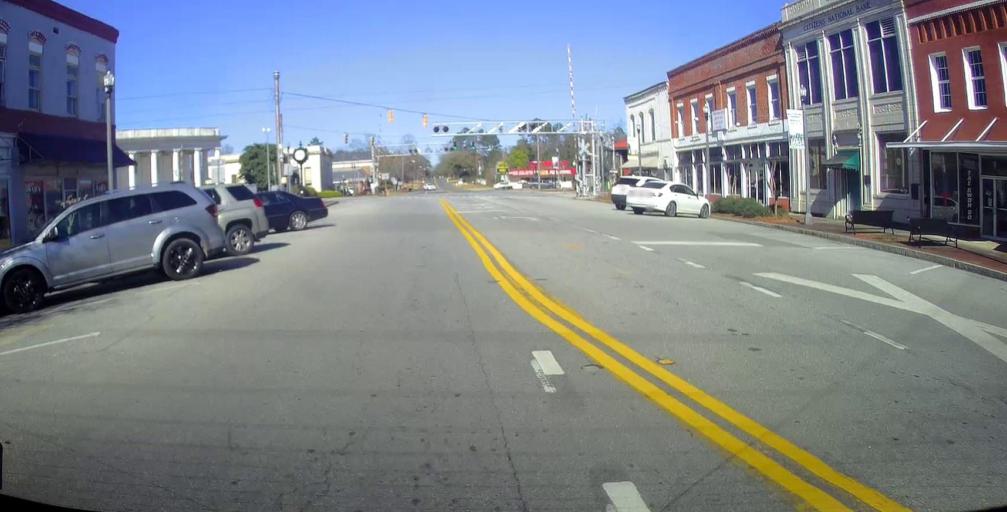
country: US
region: Georgia
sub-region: Macon County
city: Montezuma
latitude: 32.3000
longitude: -84.0303
